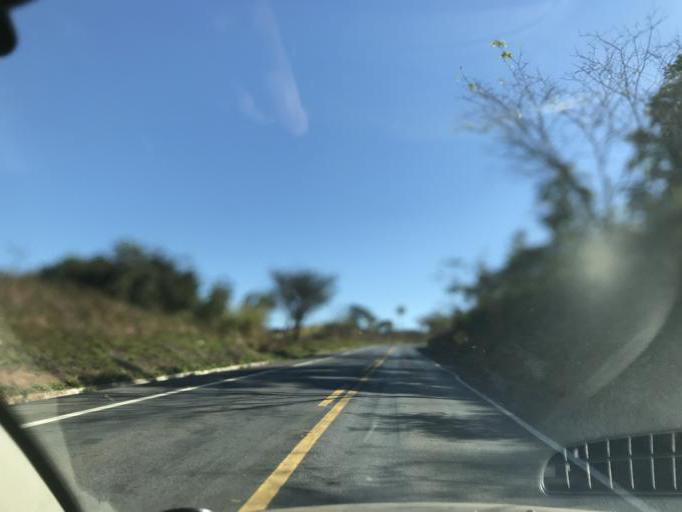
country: BR
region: Minas Gerais
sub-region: Campos Altos
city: Campos Altos
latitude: -19.8180
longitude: -46.0249
